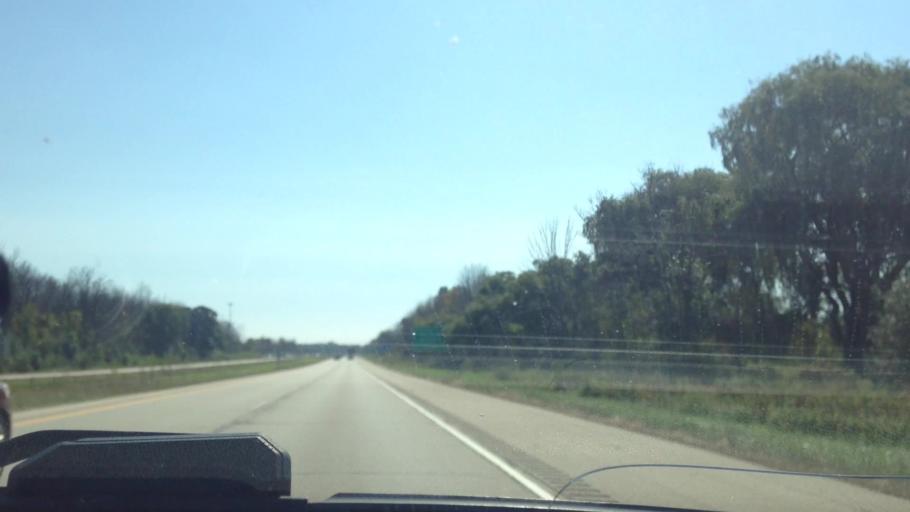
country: US
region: Wisconsin
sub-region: Ozaukee County
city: Grafton
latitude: 43.2916
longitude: -87.9209
